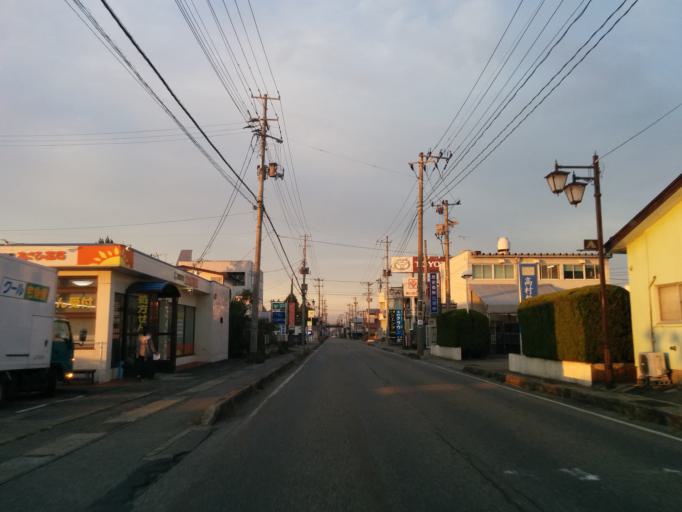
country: JP
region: Fukushima
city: Kitakata
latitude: 37.4657
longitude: 139.9225
